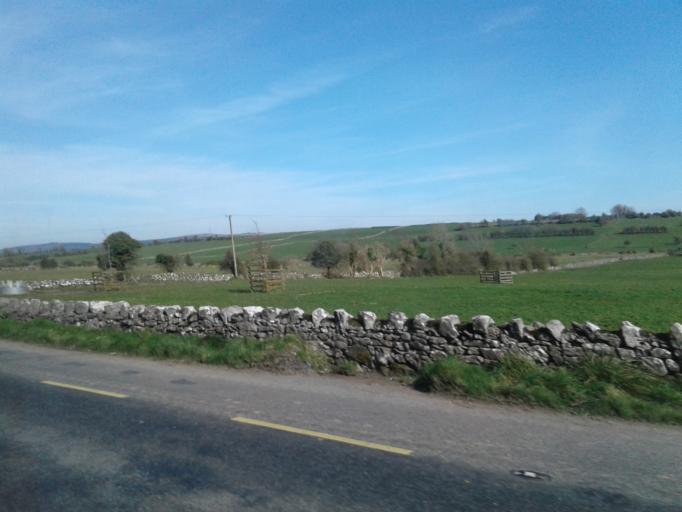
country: IE
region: Connaught
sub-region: County Galway
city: Gort
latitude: 53.1045
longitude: -8.8083
